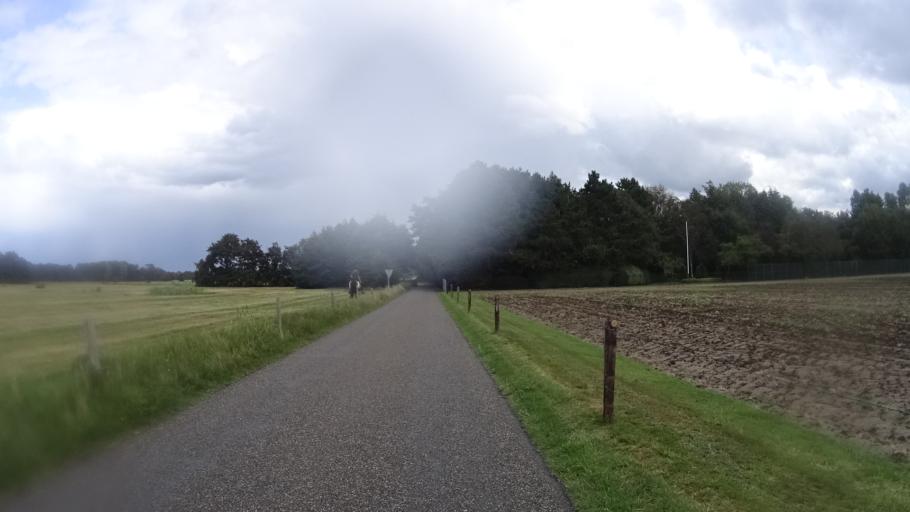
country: NL
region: North Holland
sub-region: Gemeente Bergen
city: Egmond aan Zee
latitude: 52.6555
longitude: 4.6629
